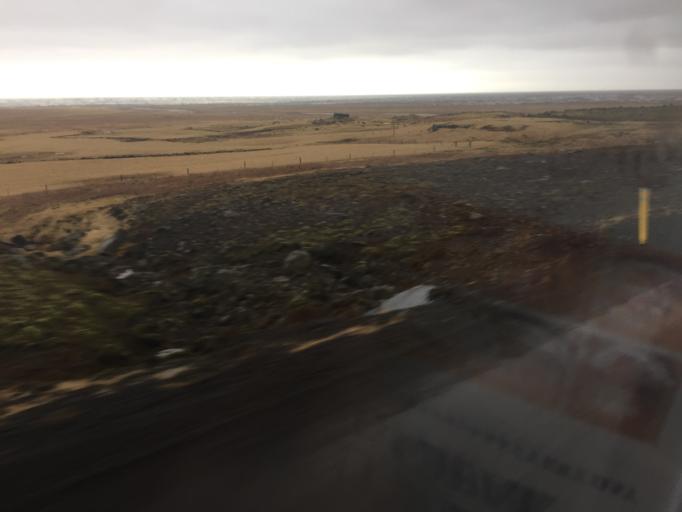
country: IS
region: East
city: Hoefn
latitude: 63.8806
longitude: -16.6761
